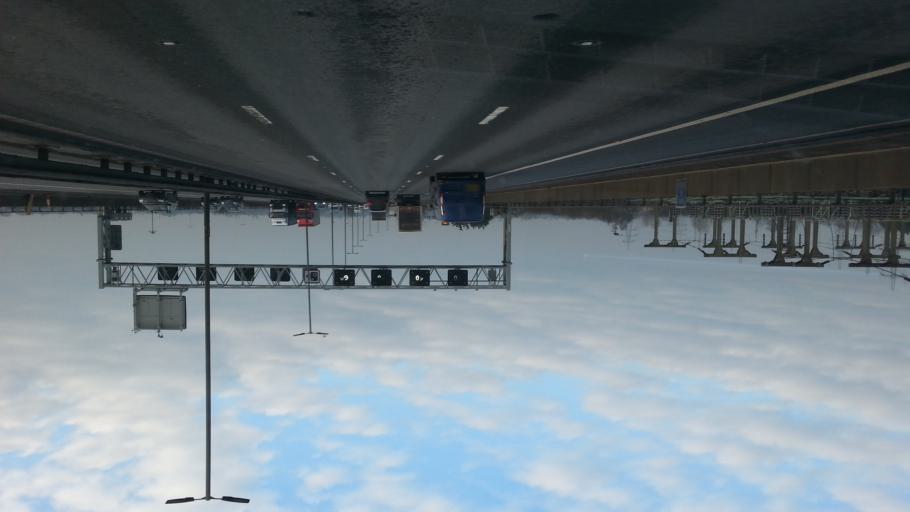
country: GB
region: England
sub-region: City and Borough of Birmingham
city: Birmingham
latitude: 52.5060
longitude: -1.8517
